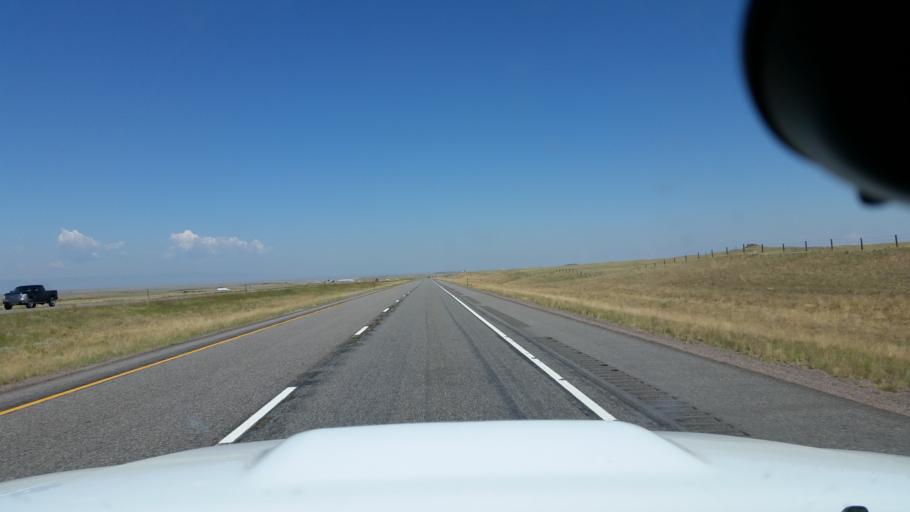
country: US
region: Wyoming
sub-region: Albany County
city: Laramie
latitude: 41.0842
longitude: -105.5110
